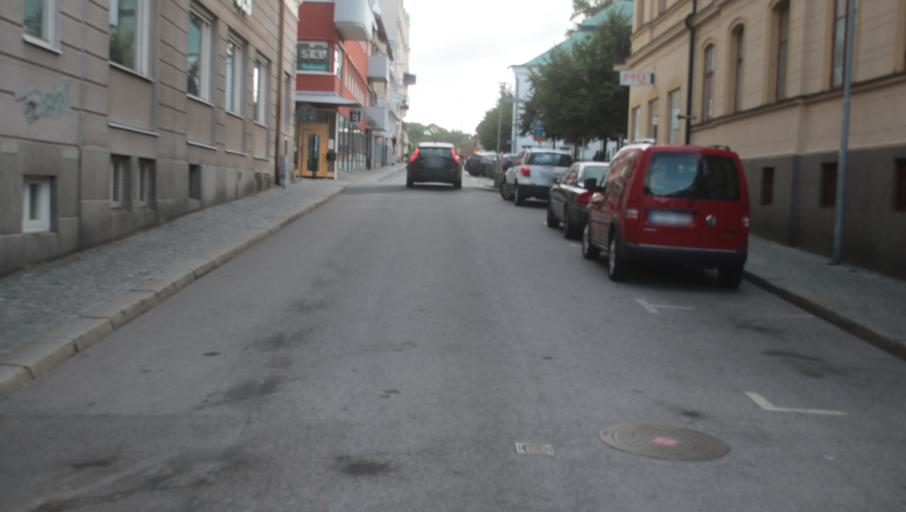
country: SE
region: Blekinge
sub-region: Karlshamns Kommun
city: Karlshamn
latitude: 56.1713
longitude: 14.8606
